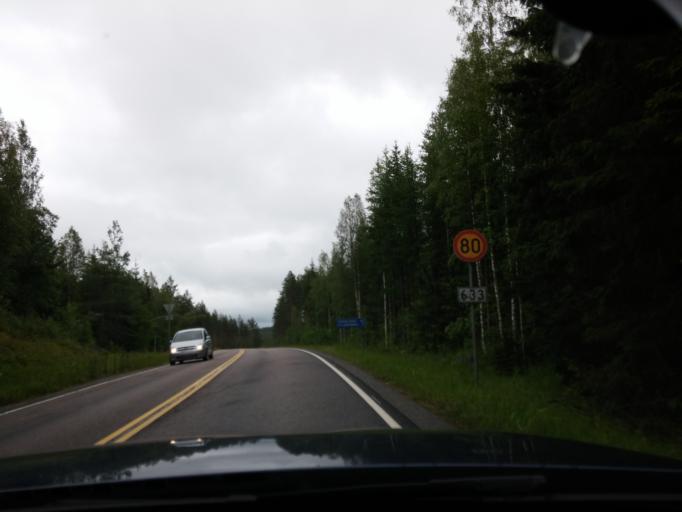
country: FI
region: Central Finland
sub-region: Saarijaervi-Viitasaari
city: Pylkoenmaeki
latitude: 62.5903
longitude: 24.5958
